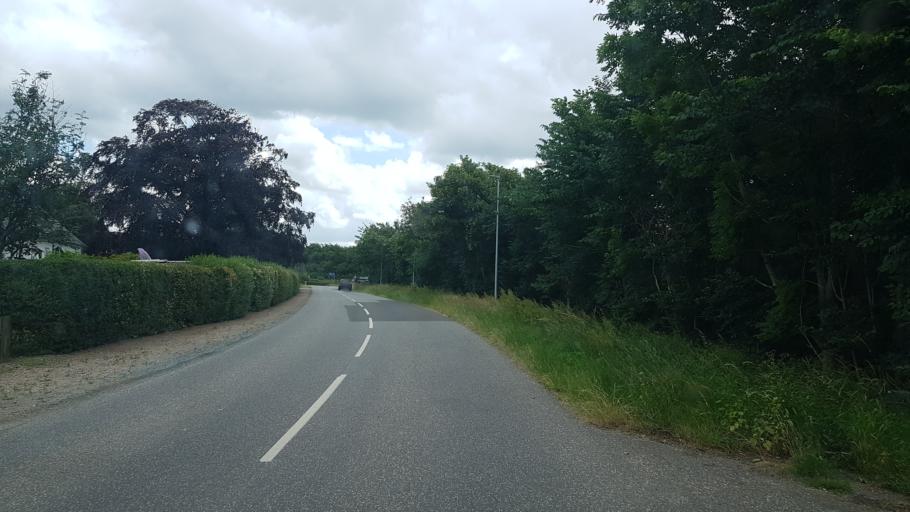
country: DK
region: South Denmark
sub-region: Kolding Kommune
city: Vamdrup
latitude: 55.4328
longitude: 9.2643
